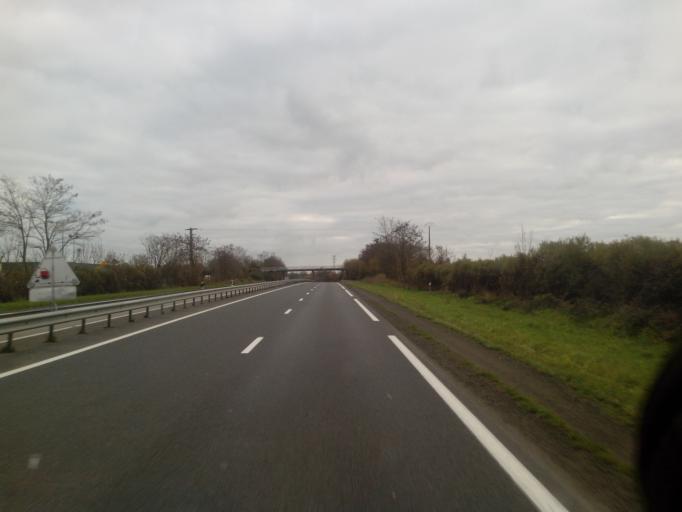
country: FR
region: Poitou-Charentes
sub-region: Departement des Deux-Sevres
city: Bressuire
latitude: 46.8449
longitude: -0.4687
